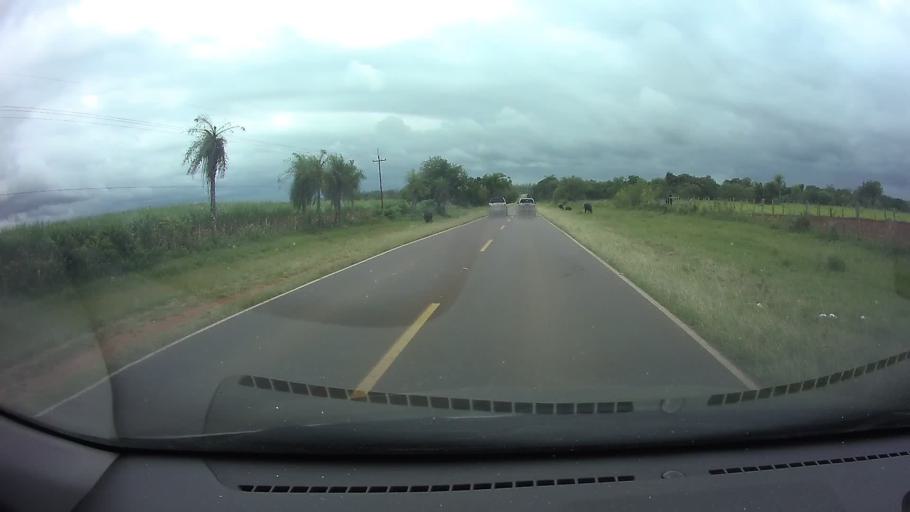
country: PY
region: Central
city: Nueva Italia
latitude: -25.5970
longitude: -57.5025
